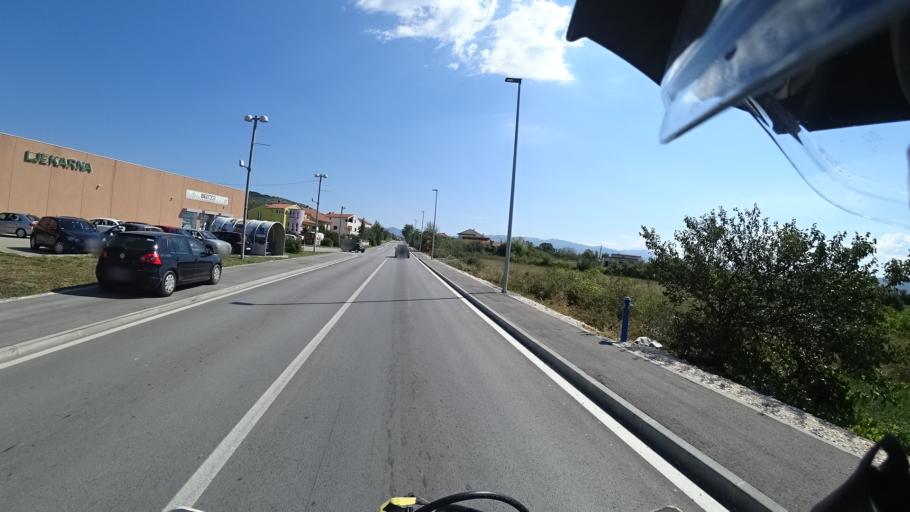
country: HR
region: Sibensko-Kniniska
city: Drnis
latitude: 43.8612
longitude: 16.1648
